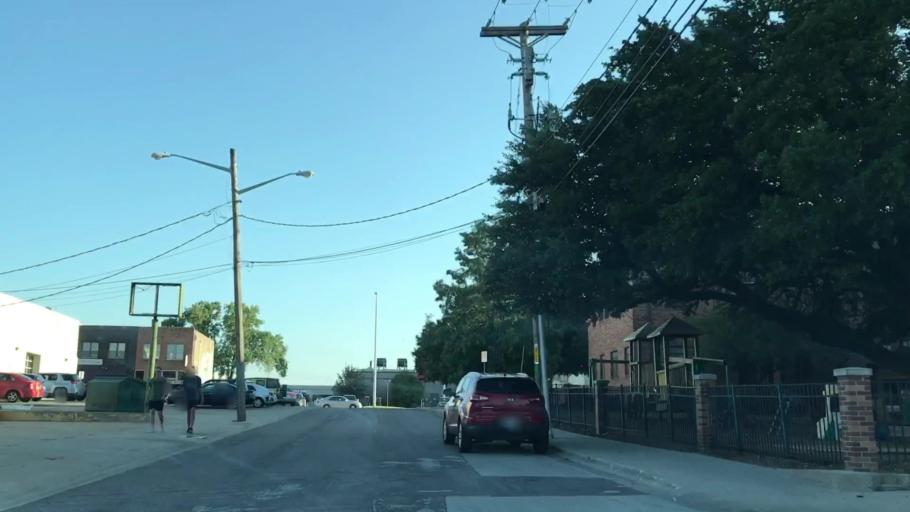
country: US
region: Texas
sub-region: Denton County
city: Denton
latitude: 33.2164
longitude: -97.1352
